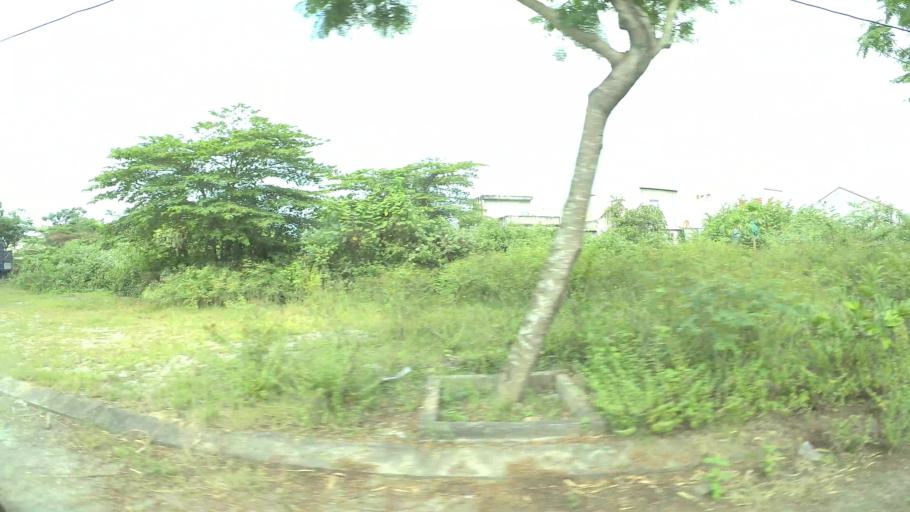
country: VN
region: Da Nang
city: Lien Chieu
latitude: 16.0576
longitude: 108.1592
